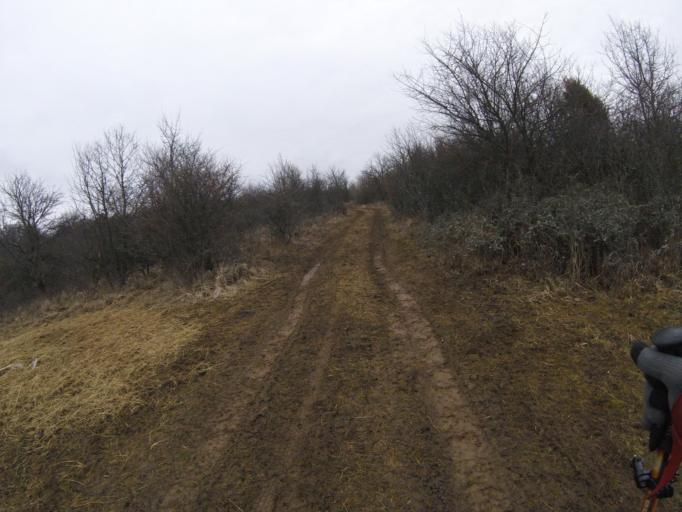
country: HU
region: Borsod-Abauj-Zemplen
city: Rudabanya
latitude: 48.4643
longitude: 20.6021
